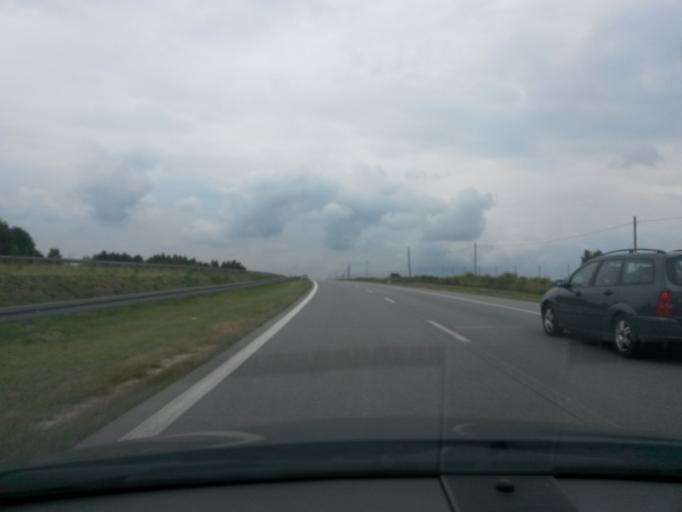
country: PL
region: Lodz Voivodeship
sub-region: Powiat skierniewicki
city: Kowiesy
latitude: 51.8756
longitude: 20.3880
